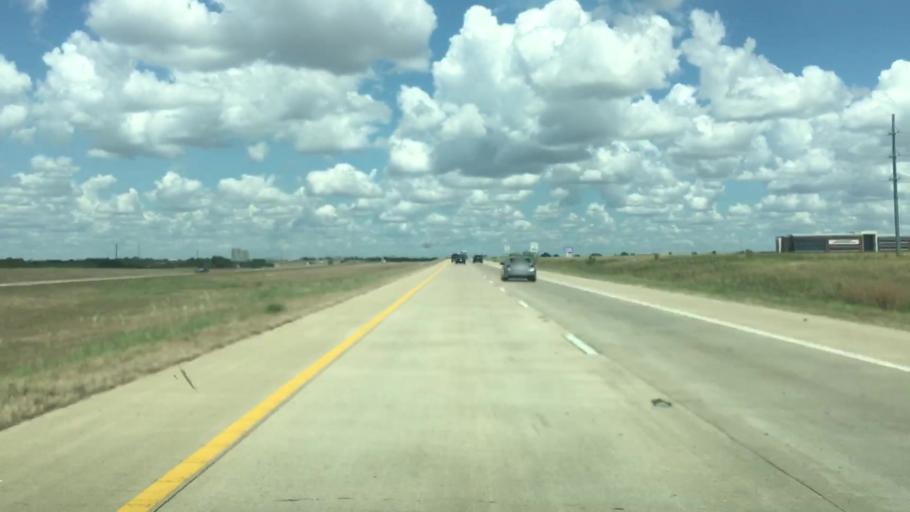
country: US
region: Texas
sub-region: Williamson County
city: Hutto
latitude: 30.5481
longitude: -97.5764
